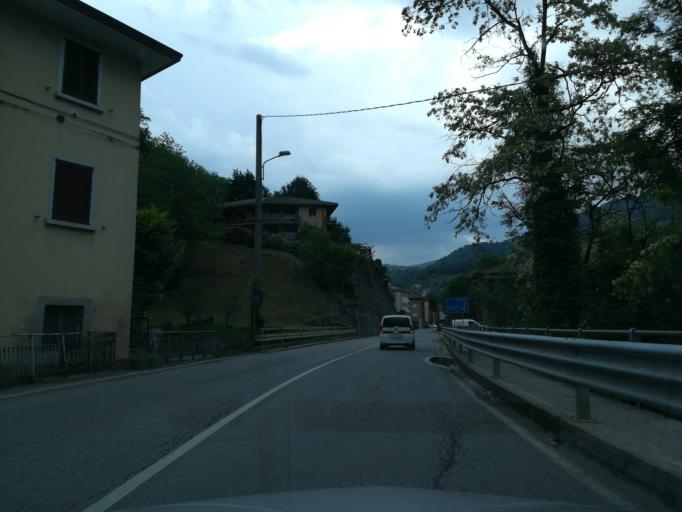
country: IT
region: Lombardy
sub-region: Provincia di Bergamo
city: Camoneone
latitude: 45.7823
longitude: 9.5736
